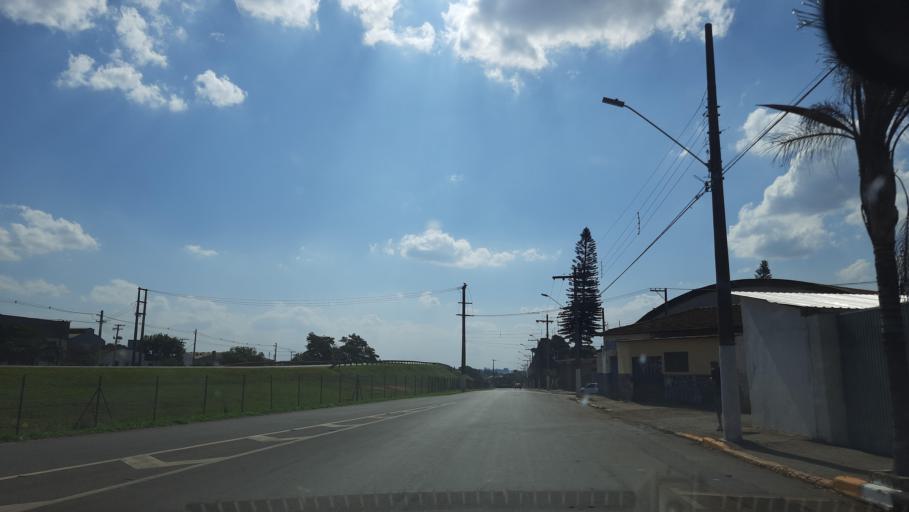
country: BR
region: Sao Paulo
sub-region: Vargem Grande Do Sul
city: Vargem Grande do Sul
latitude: -21.8412
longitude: -46.9064
